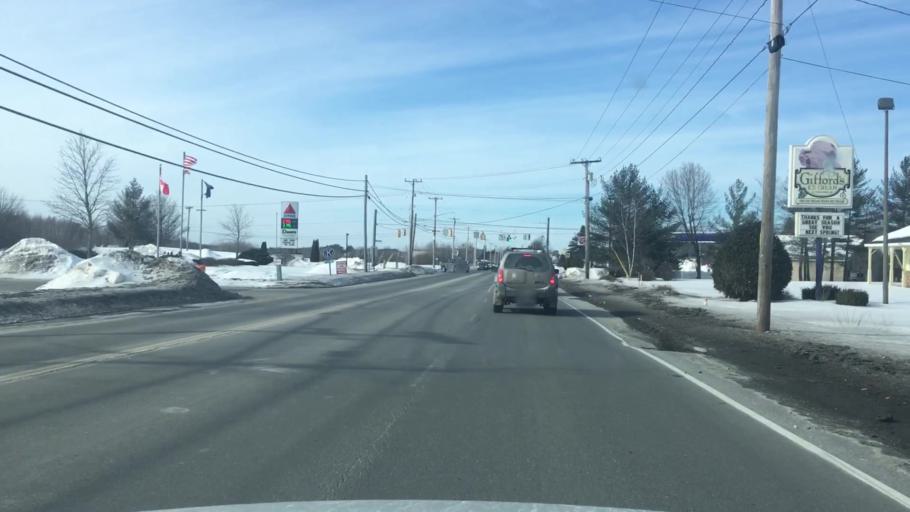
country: US
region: Maine
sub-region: Penobscot County
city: Bangor
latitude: 44.8353
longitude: -68.7906
